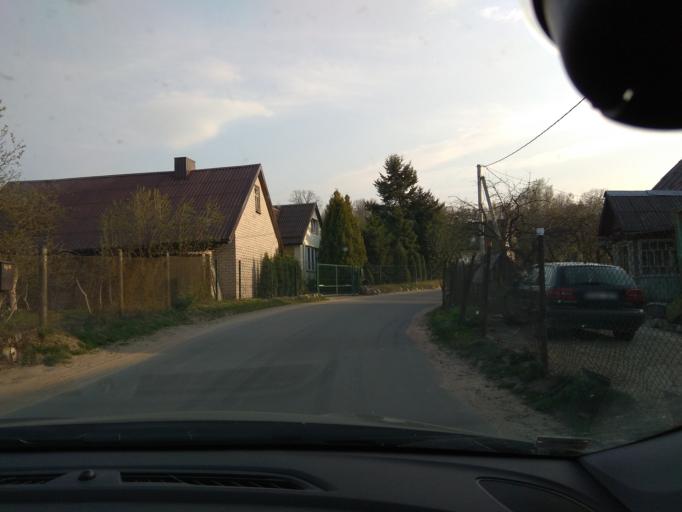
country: LT
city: Baltoji Voke
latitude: 54.5949
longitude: 25.1753
